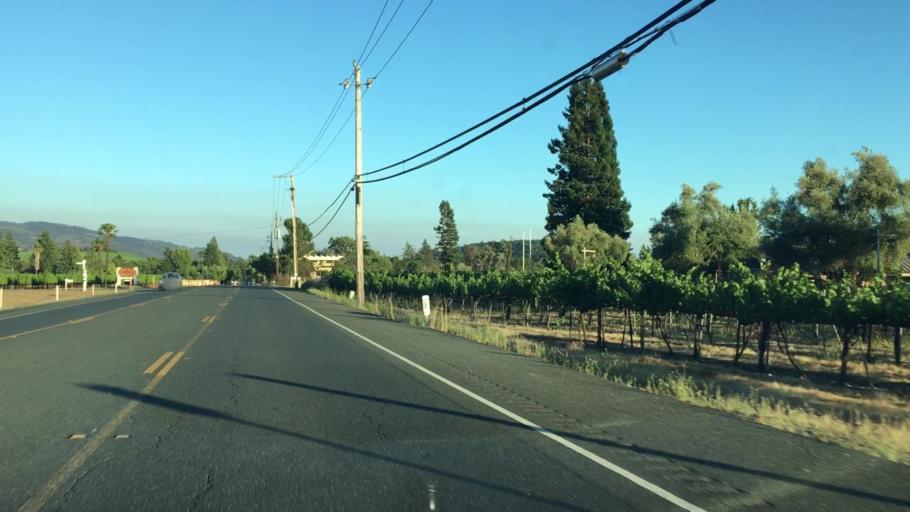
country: US
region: California
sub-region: Sonoma County
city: Kenwood
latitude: 38.4240
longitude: -122.5560
